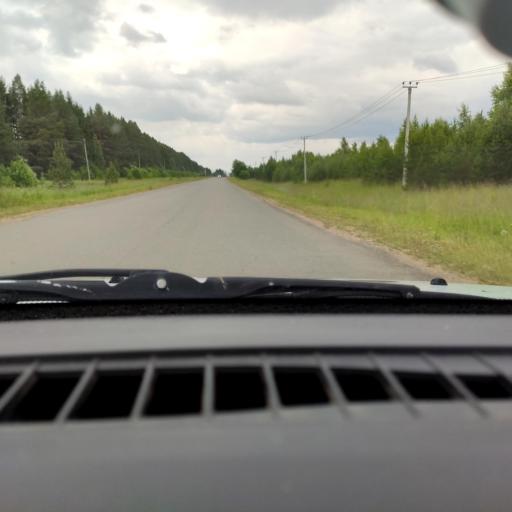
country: RU
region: Perm
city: Uinskoye
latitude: 57.1088
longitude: 56.6622
